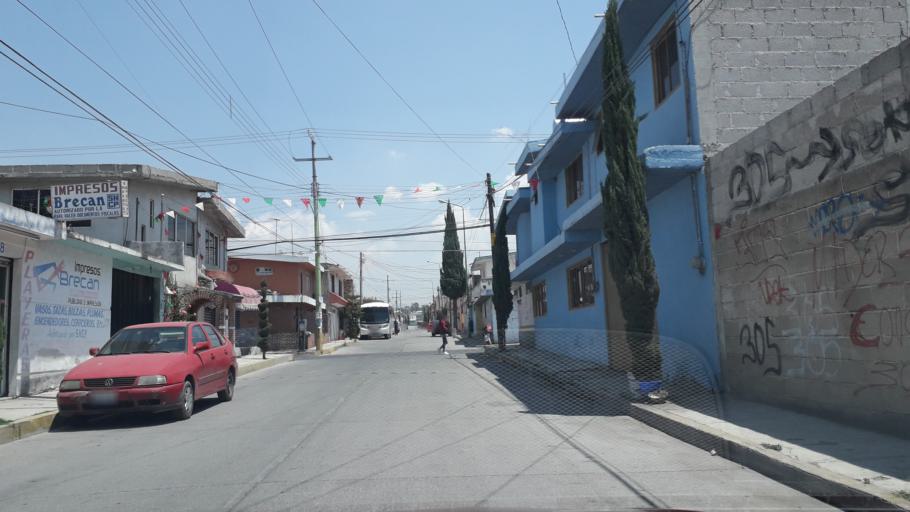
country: MX
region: Puebla
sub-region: Puebla
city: Primero de Mayo
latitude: 19.0691
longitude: -98.1187
